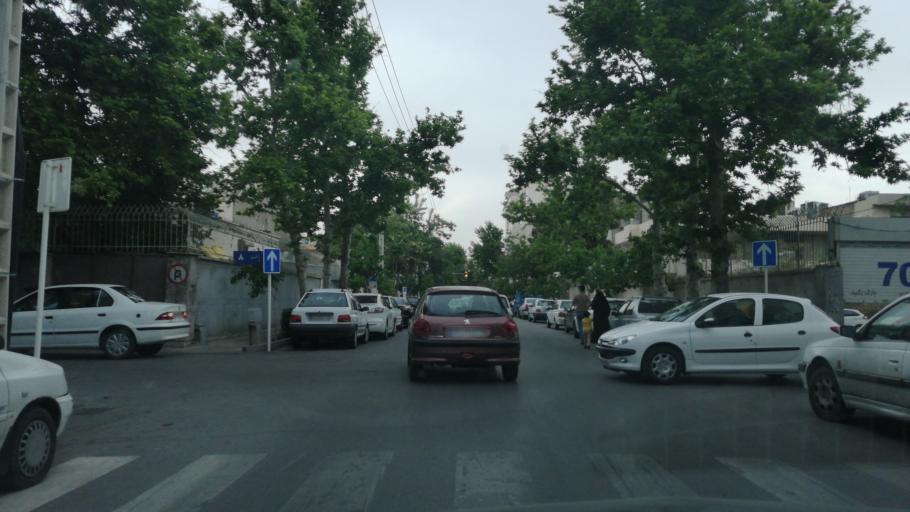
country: IR
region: Razavi Khorasan
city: Mashhad
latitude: 36.2954
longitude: 59.5817
